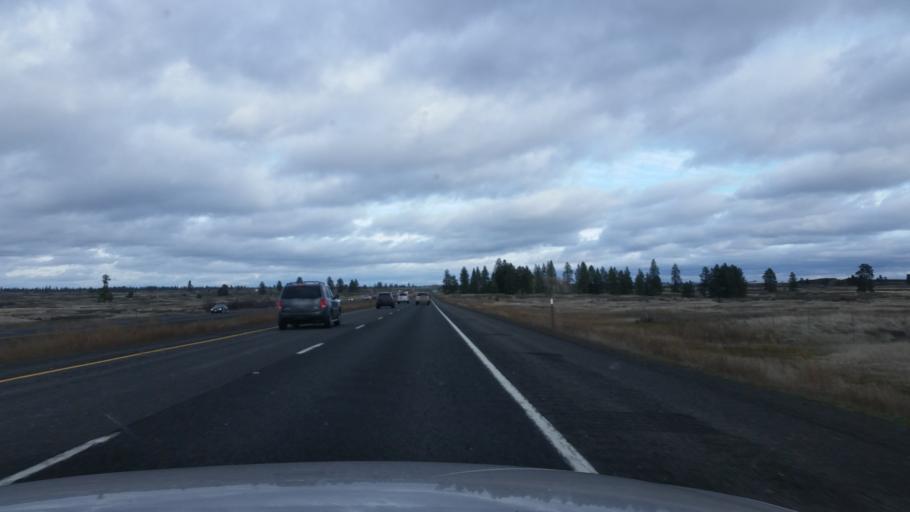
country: US
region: Washington
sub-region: Spokane County
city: Medical Lake
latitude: 47.3879
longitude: -117.8535
